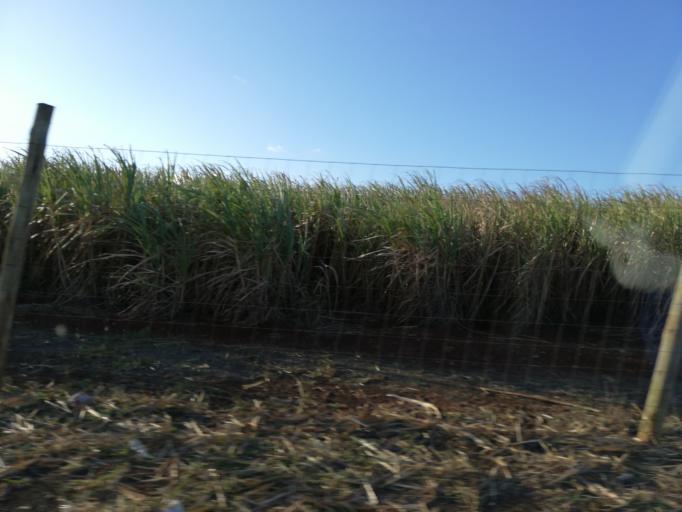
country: MU
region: Pamplemousses
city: Grande Pointe aux Piments
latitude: -20.0805
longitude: 57.5306
